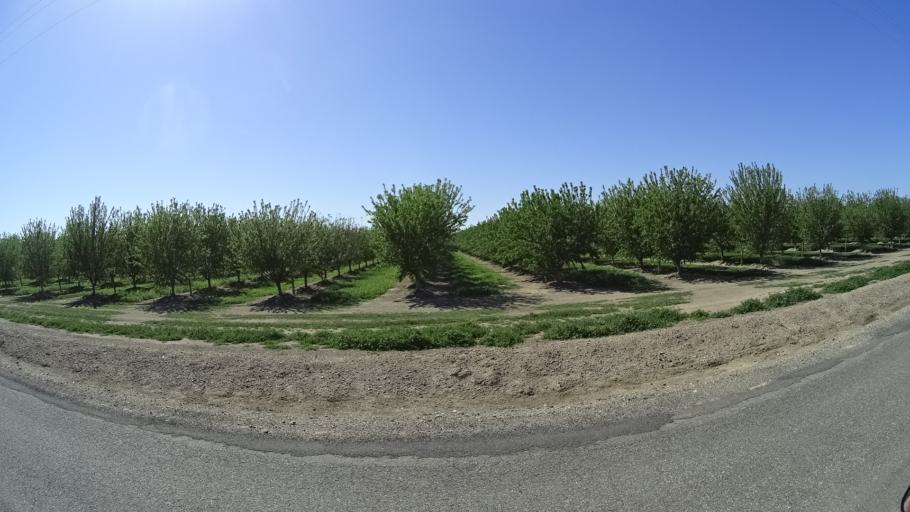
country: US
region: California
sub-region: Glenn County
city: Orland
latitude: 39.6972
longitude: -122.2433
